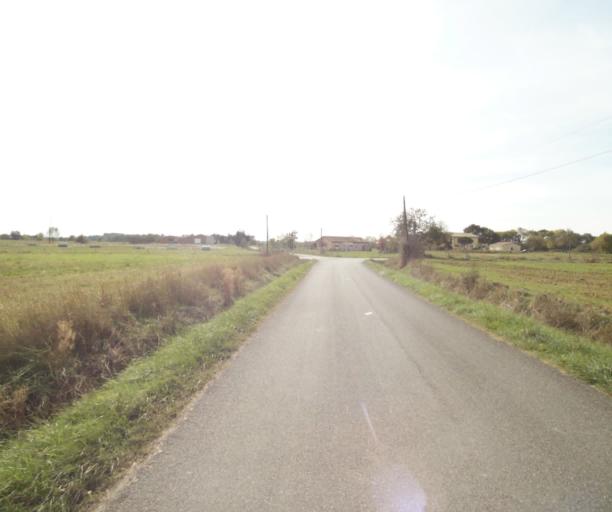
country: FR
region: Midi-Pyrenees
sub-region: Departement du Tarn-et-Garonne
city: Labastide-Saint-Pierre
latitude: 43.9051
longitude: 1.3849
